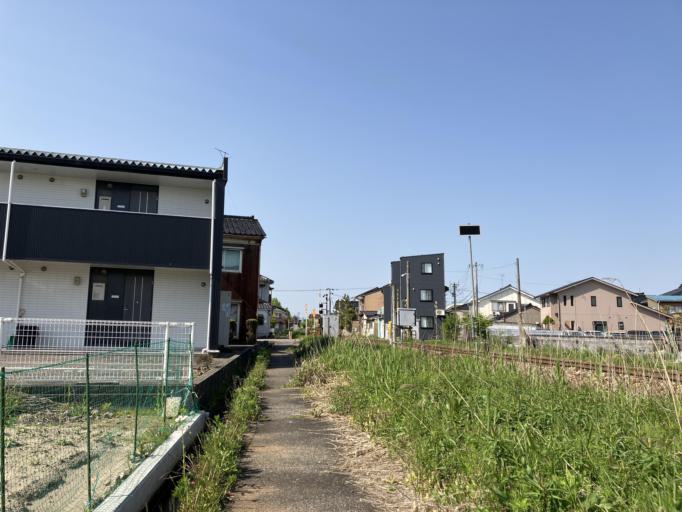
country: JP
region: Toyama
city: Takaoka
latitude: 36.7454
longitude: 137.0256
